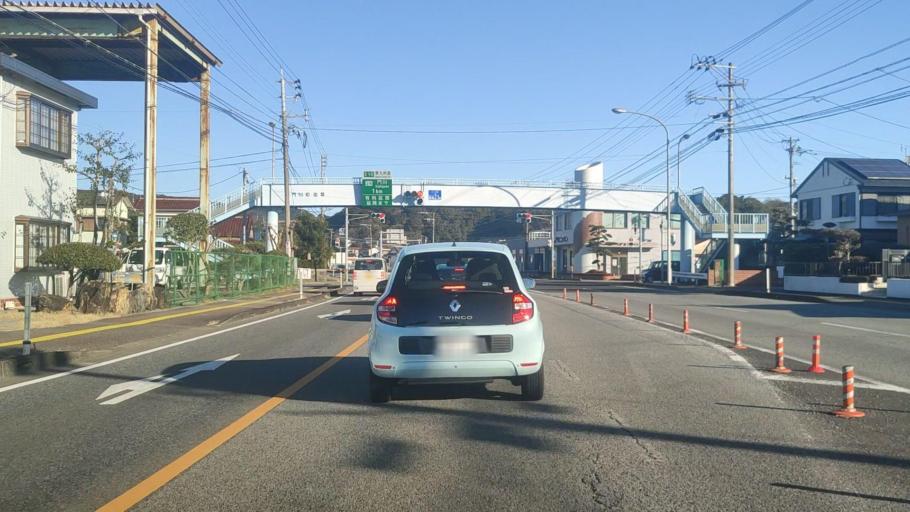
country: JP
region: Miyazaki
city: Nobeoka
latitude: 32.4877
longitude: 131.6642
